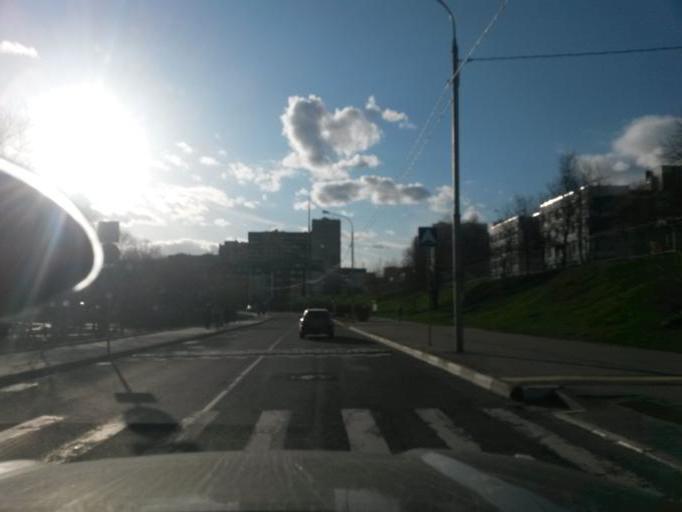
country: RU
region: Moscow
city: Annino
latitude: 55.5731
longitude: 37.5880
